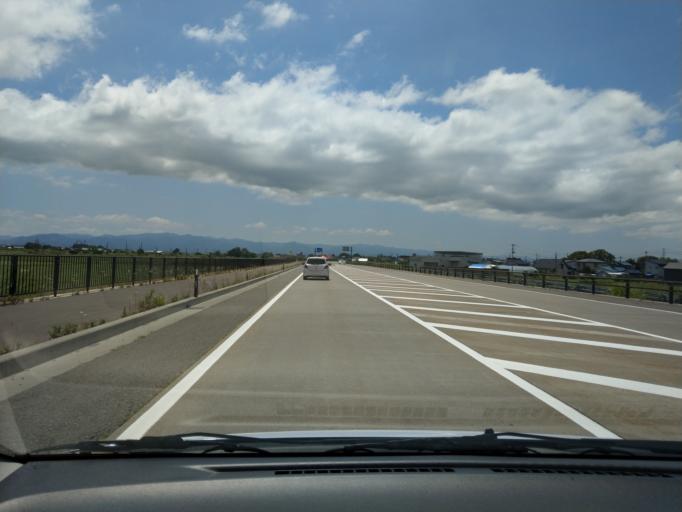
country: JP
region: Aomori
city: Namioka
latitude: 40.6945
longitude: 140.5639
